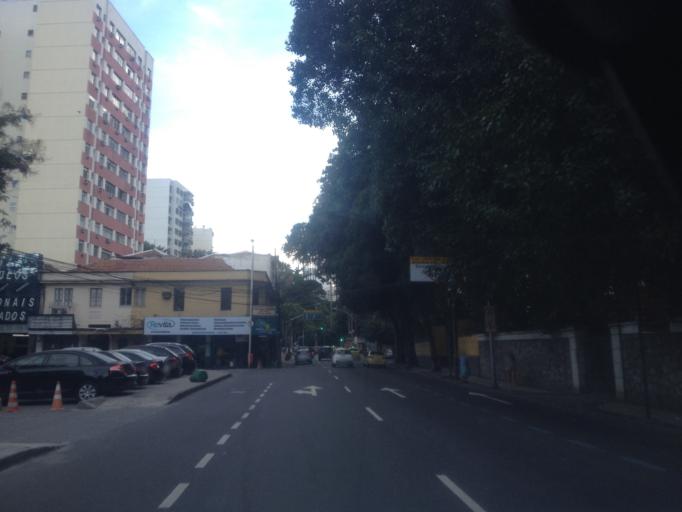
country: BR
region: Rio de Janeiro
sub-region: Rio De Janeiro
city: Rio de Janeiro
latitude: -22.9510
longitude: -43.1938
